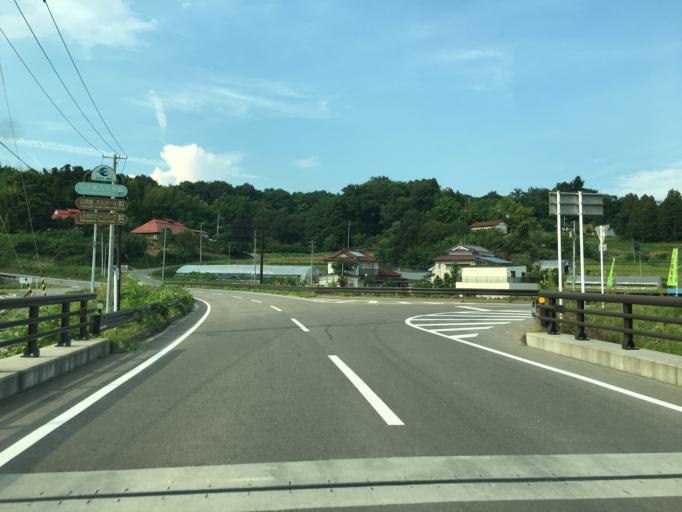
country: JP
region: Fukushima
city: Motomiya
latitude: 37.4818
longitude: 140.4146
